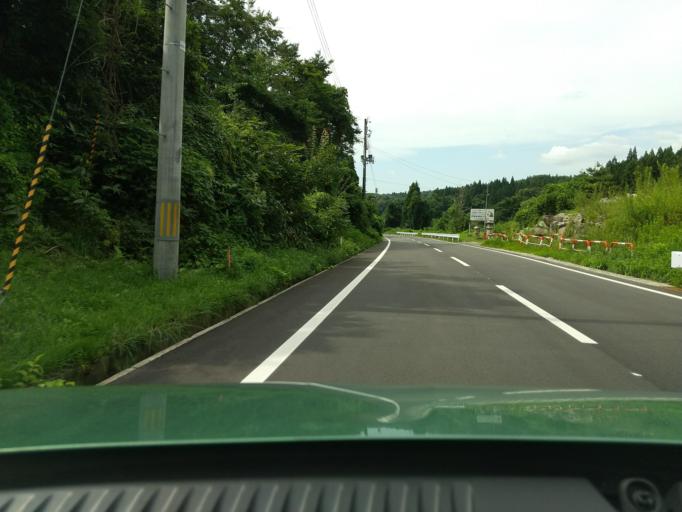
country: JP
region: Akita
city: Akita
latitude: 39.7196
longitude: 140.1883
